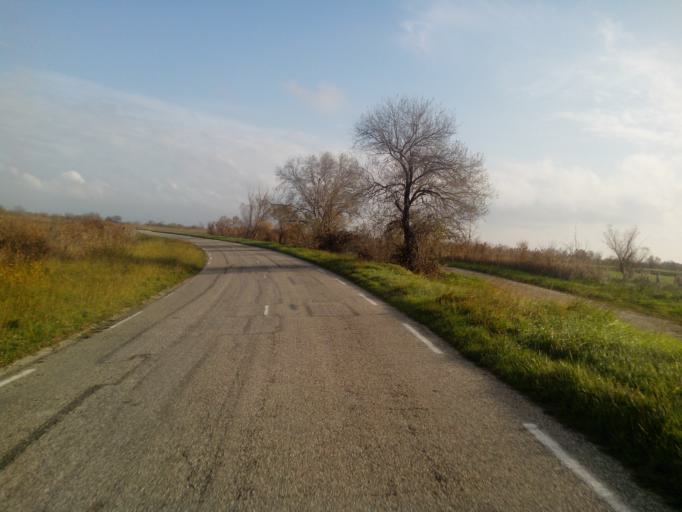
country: FR
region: Provence-Alpes-Cote d'Azur
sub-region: Departement des Bouches-du-Rhone
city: Arles
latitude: 43.5709
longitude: 4.5314
